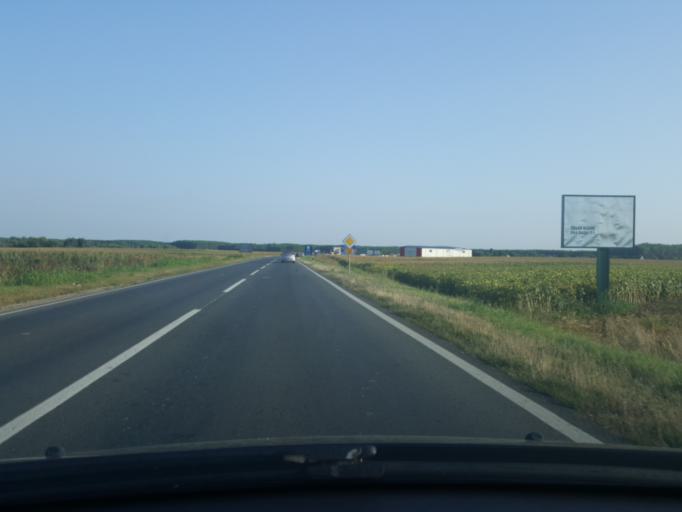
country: RS
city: Klenak
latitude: 44.7719
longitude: 19.7258
